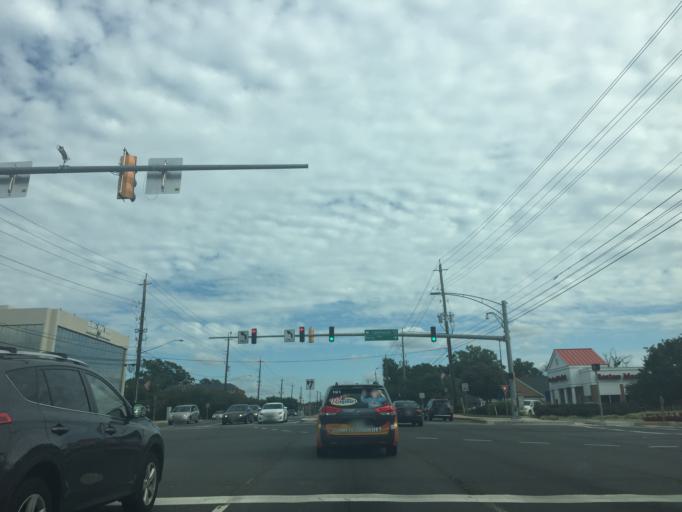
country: US
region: Maryland
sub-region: Montgomery County
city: Gaithersburg
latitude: 39.1502
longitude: -77.2094
